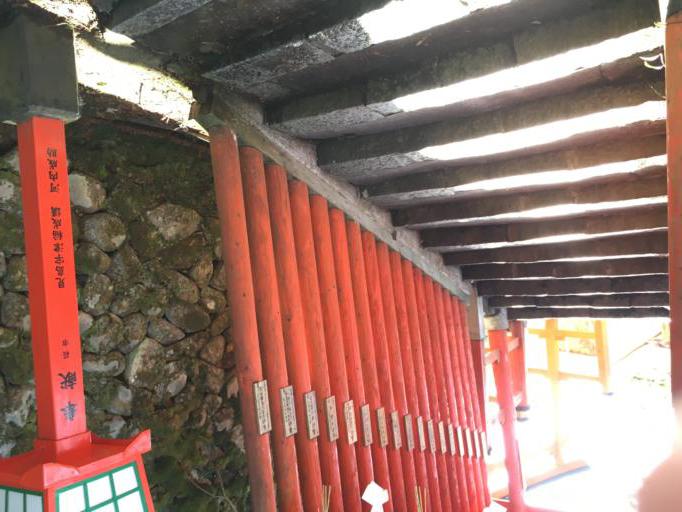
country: JP
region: Shimane
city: Masuda
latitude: 34.4657
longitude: 131.7698
